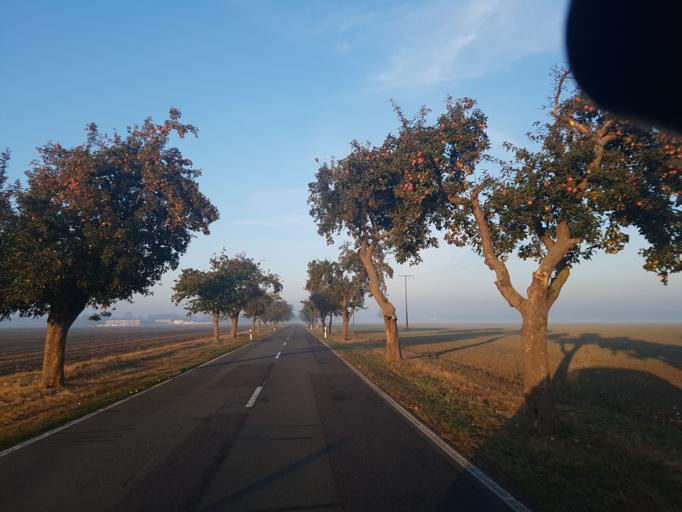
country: DE
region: Brandenburg
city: Juterbog
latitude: 51.8979
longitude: 13.0842
